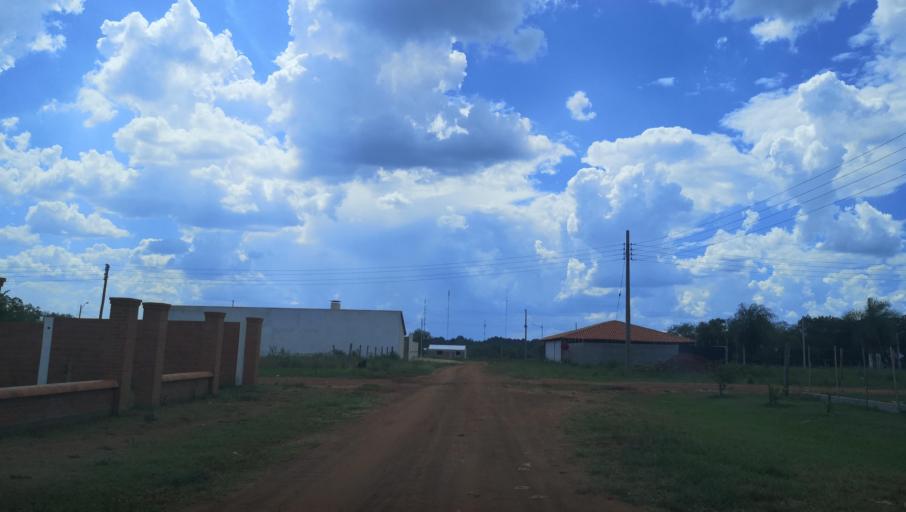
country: PY
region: Misiones
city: Santa Maria
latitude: -26.8970
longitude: -57.0409
